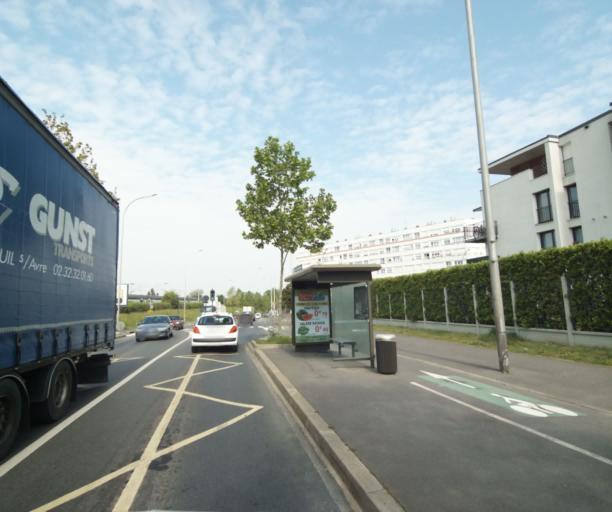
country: FR
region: Ile-de-France
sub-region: Departement du Val-d'Oise
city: Cormeilles-en-Parisis
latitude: 48.9508
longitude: 2.2221
